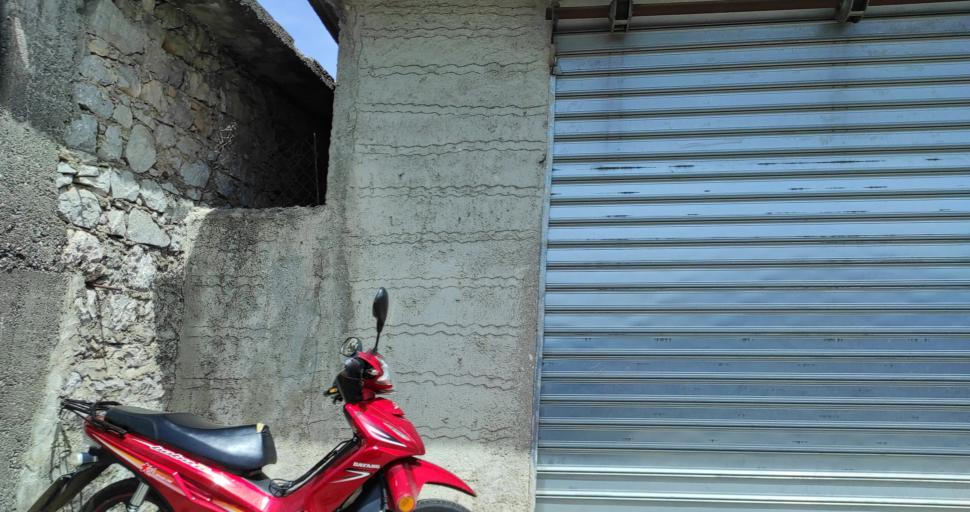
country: AL
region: Shkoder
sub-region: Rrethi i Malesia e Madhe
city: Gruemire
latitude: 42.1200
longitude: 19.5733
